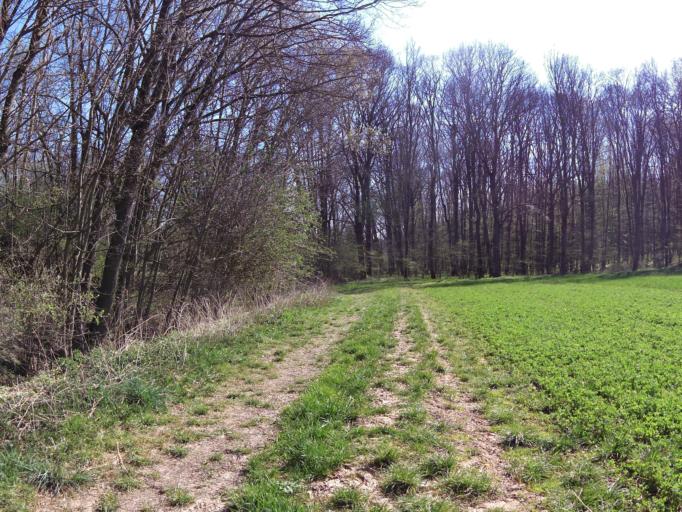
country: DE
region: Bavaria
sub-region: Regierungsbezirk Unterfranken
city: Kurnach
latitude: 49.8284
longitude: 10.0486
